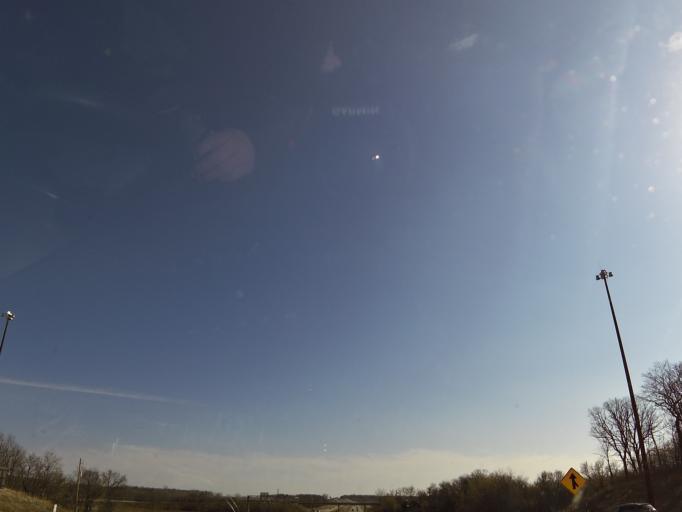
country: US
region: Minnesota
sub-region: Steele County
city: Owatonna
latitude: 44.0555
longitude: -93.2500
